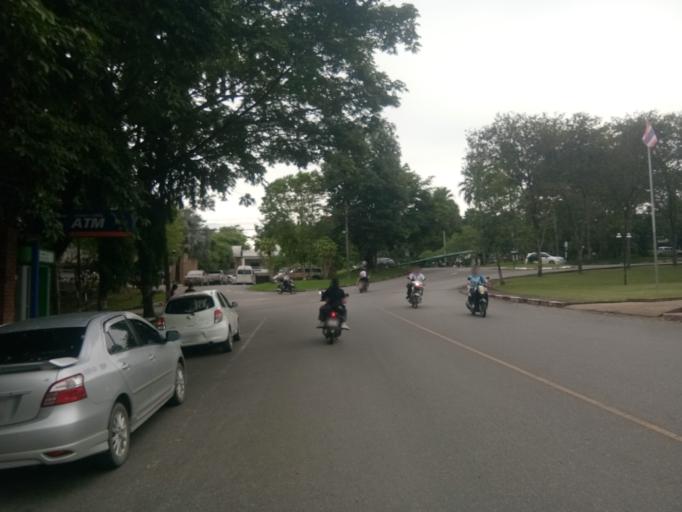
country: TH
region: Chiang Rai
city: Chiang Rai
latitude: 19.9800
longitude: 99.8509
